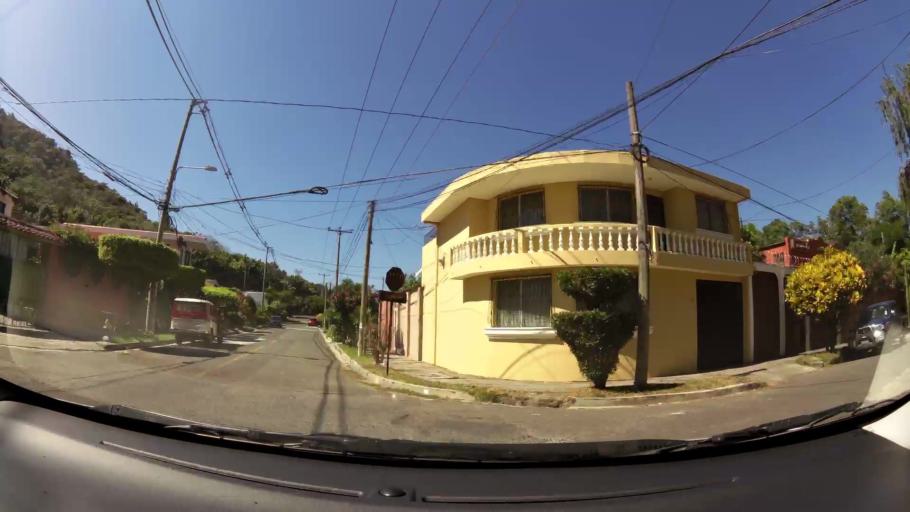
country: SV
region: La Libertad
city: Santa Tecla
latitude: 13.6662
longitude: -89.2816
